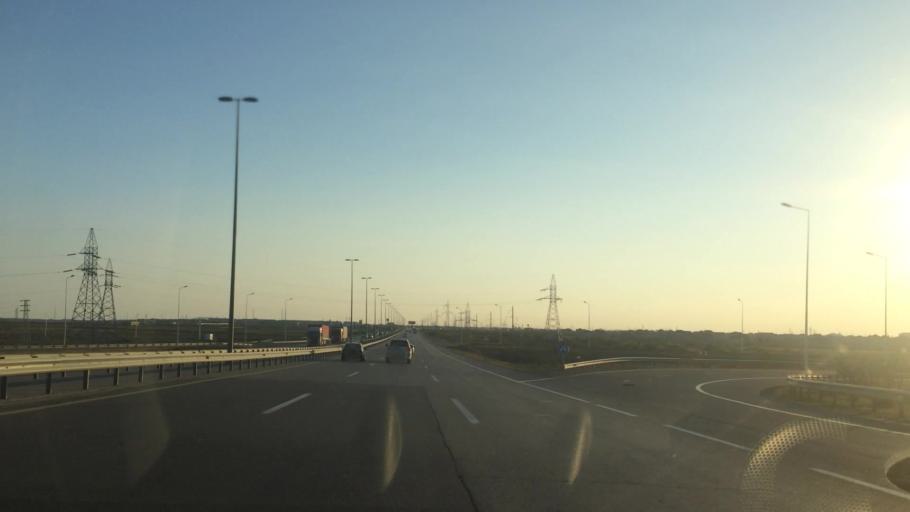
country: AZ
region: Baki
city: Qobustan
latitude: 39.9806
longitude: 49.4231
